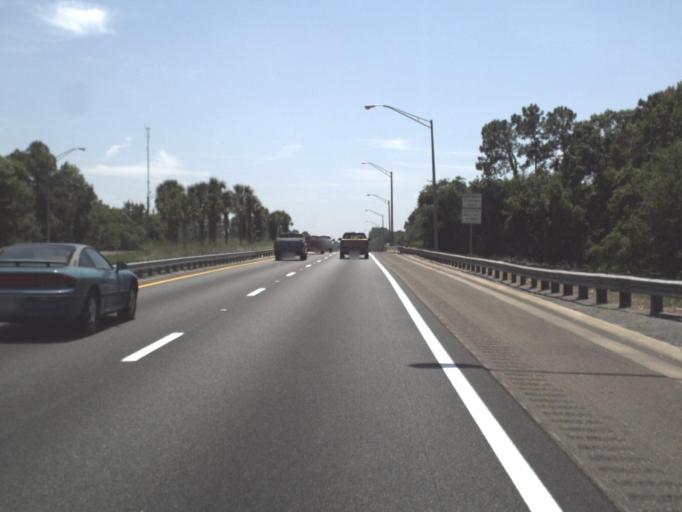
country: US
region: Florida
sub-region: Duval County
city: Jacksonville
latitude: 30.3624
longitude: -81.7611
